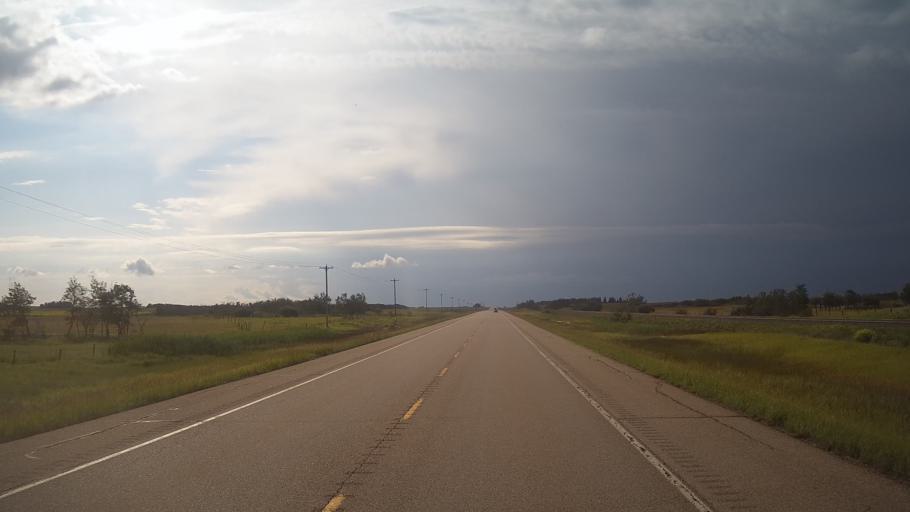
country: CA
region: Alberta
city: Viking
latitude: 53.1550
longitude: -111.9854
